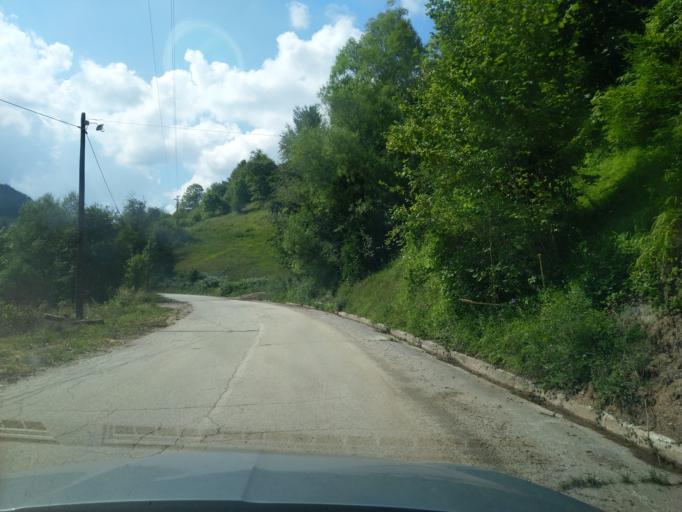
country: RS
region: Central Serbia
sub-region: Zlatiborski Okrug
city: Nova Varos
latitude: 43.5880
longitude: 19.8680
